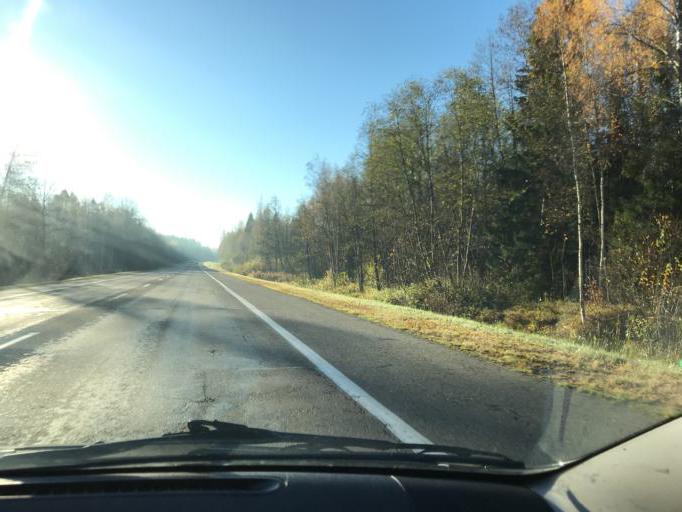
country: BY
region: Vitebsk
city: Vitebsk
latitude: 54.8947
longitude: 30.3806
